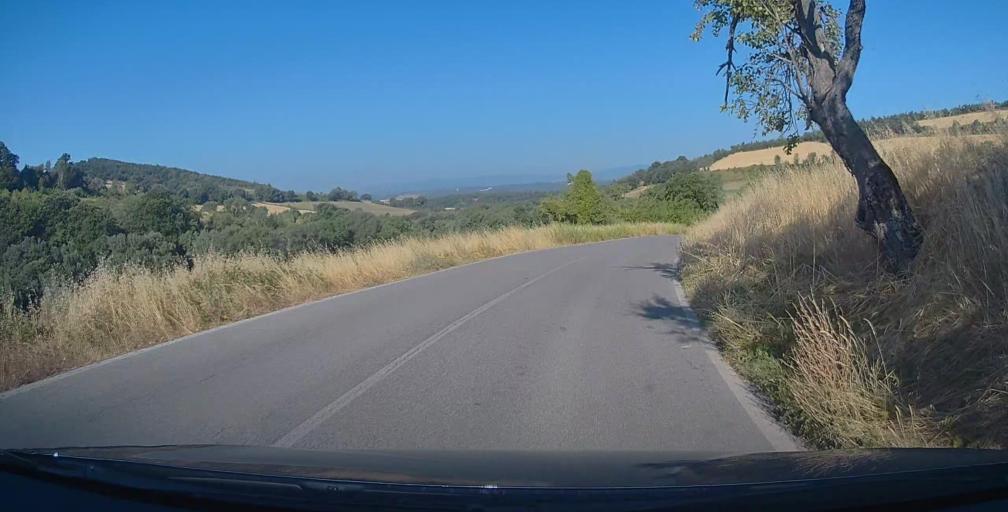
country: IT
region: Umbria
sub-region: Provincia di Terni
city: Otricoli
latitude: 42.3997
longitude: 12.4907
